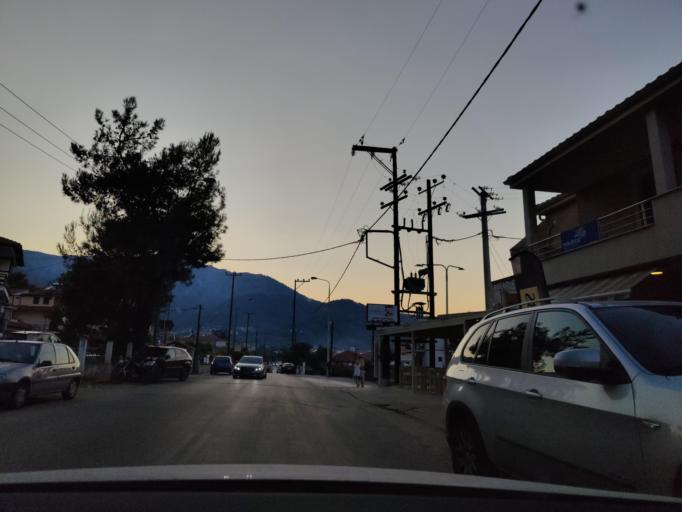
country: GR
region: East Macedonia and Thrace
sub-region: Nomos Kavalas
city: Potamia
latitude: 40.7080
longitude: 24.7576
